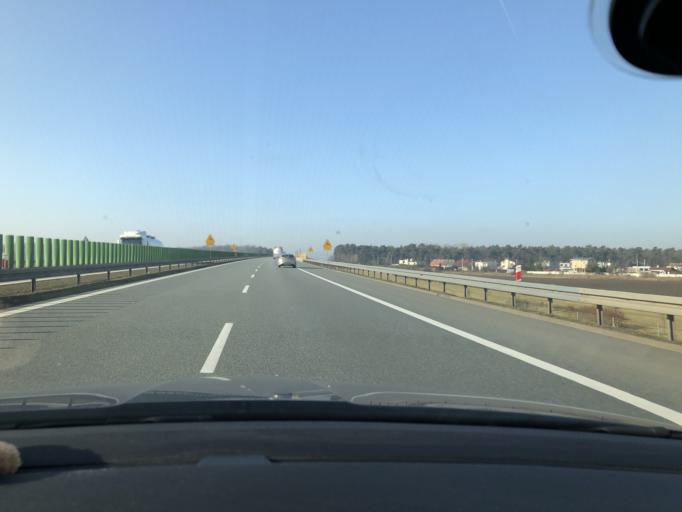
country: PL
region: Greater Poland Voivodeship
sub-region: Powiat poznanski
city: Dopiewo
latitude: 52.3485
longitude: 16.6727
